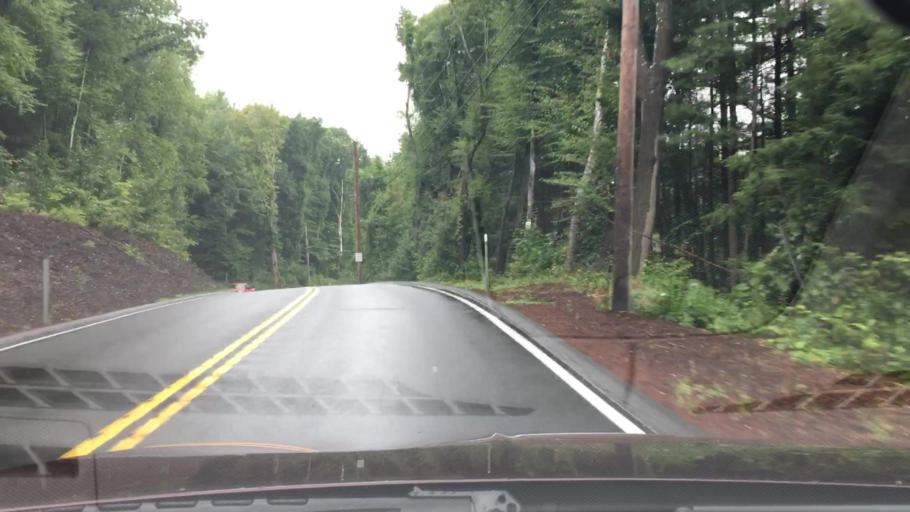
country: US
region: Connecticut
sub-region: Hartford County
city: Tariffville
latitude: 41.9451
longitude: -72.7427
